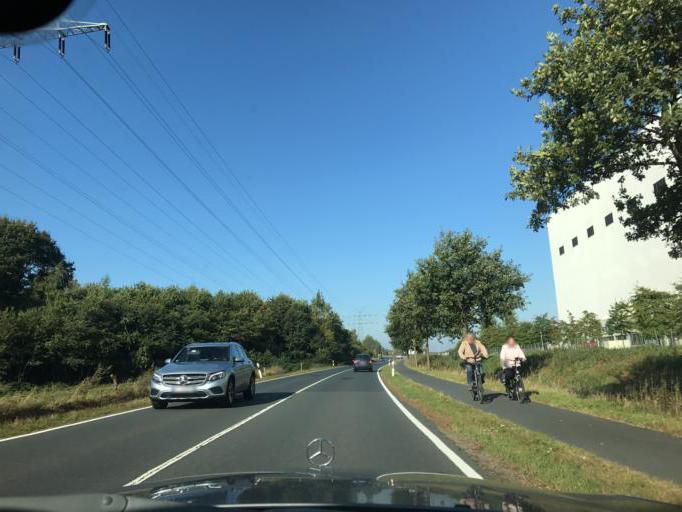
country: DE
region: Lower Saxony
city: Papenburg
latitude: 53.0955
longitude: 7.3547
